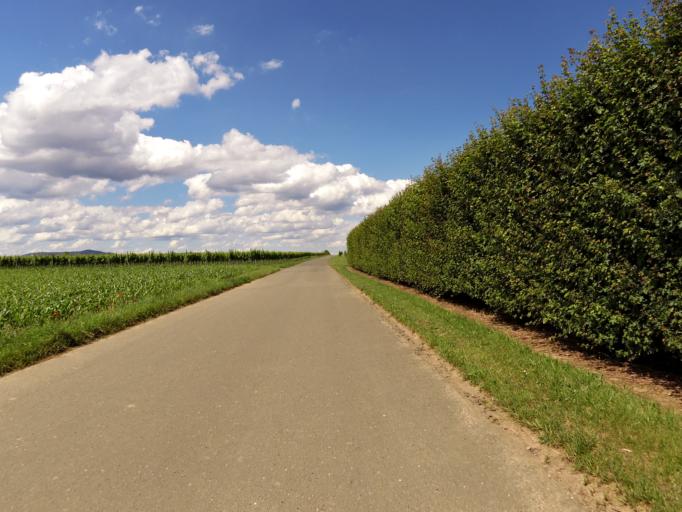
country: DE
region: Rheinland-Pfalz
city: Altdorf
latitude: 49.2881
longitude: 8.2153
